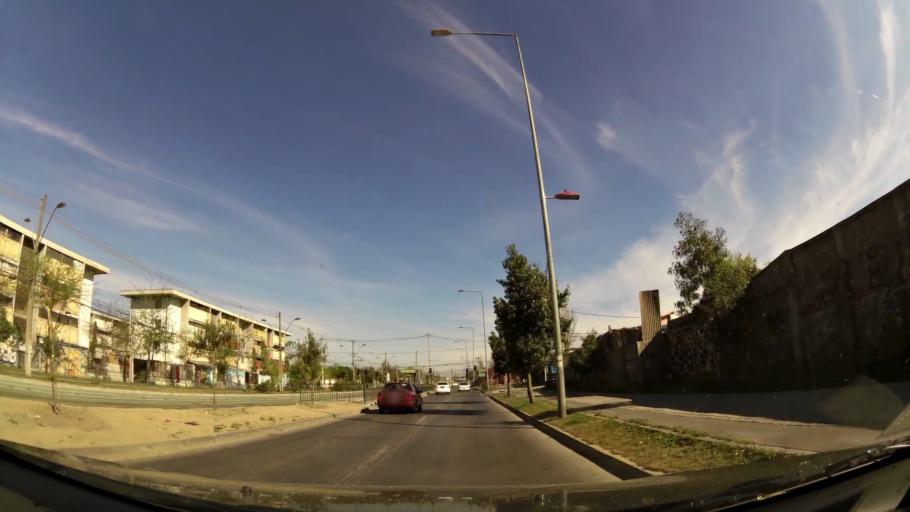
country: CL
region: Santiago Metropolitan
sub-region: Provincia de Santiago
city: Santiago
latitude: -33.4896
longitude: -70.6297
